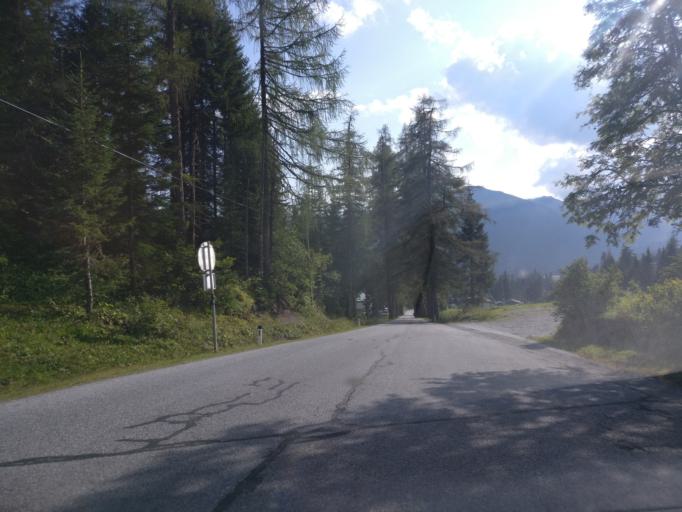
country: AT
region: Salzburg
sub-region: Politischer Bezirk Sankt Johann im Pongau
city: Muhlbach am Hochkonig
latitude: 47.4060
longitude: 13.1236
